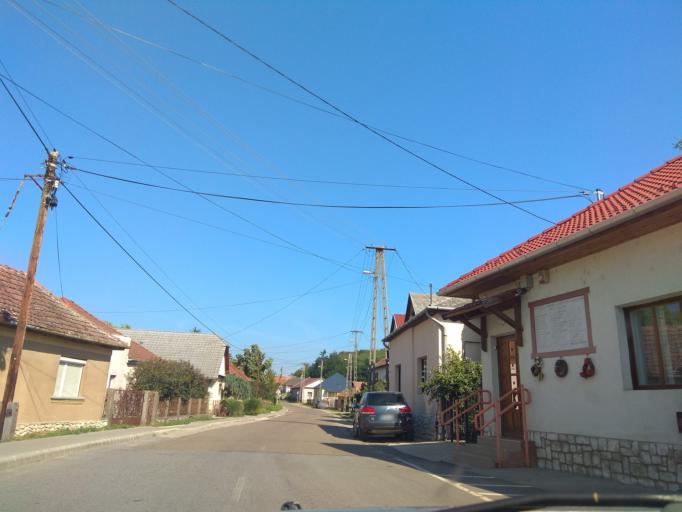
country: HU
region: Borsod-Abauj-Zemplen
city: Harsany
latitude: 47.9854
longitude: 20.7808
